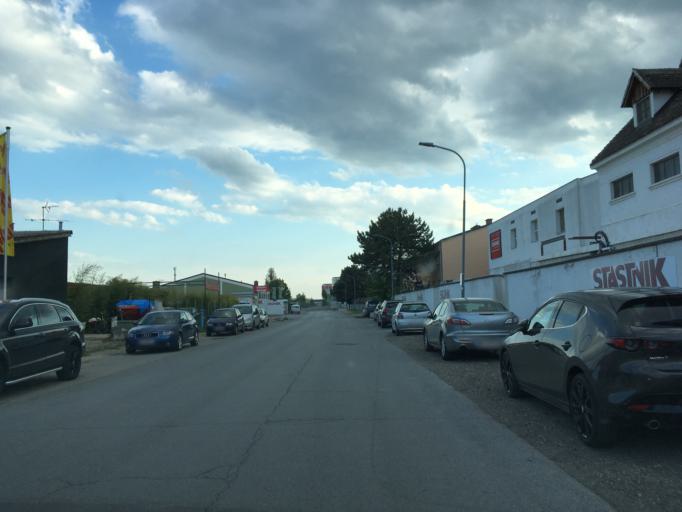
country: AT
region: Lower Austria
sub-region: Politischer Bezirk Wien-Umgebung
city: Gerasdorf bei Wien
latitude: 48.2835
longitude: 16.4816
